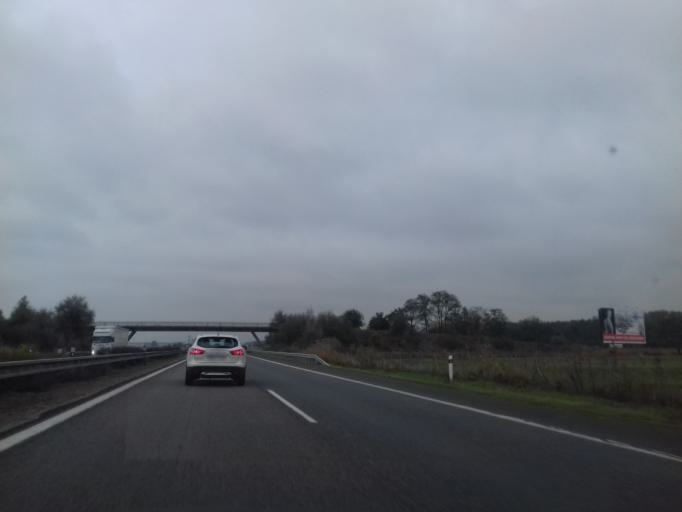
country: SK
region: Bratislavsky
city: Stupava
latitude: 48.2978
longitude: 17.0130
